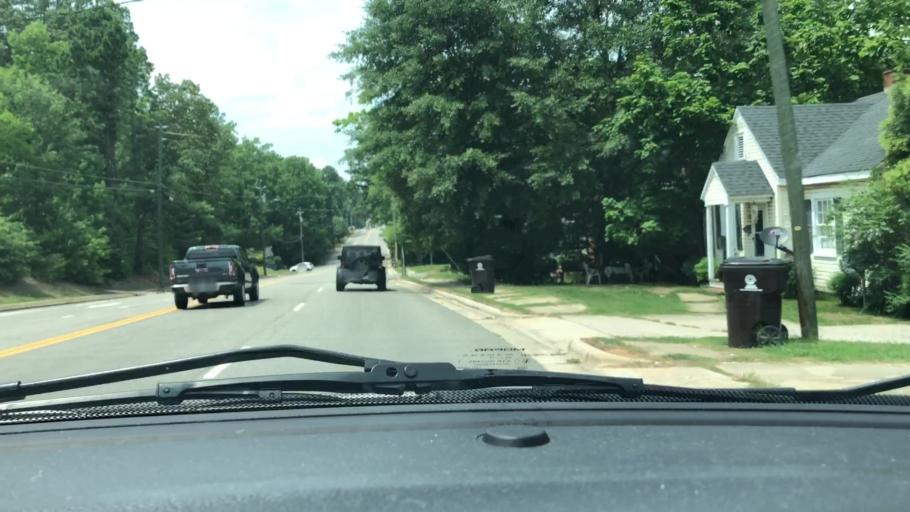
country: US
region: North Carolina
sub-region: Lee County
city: Sanford
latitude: 35.4860
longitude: -79.1856
